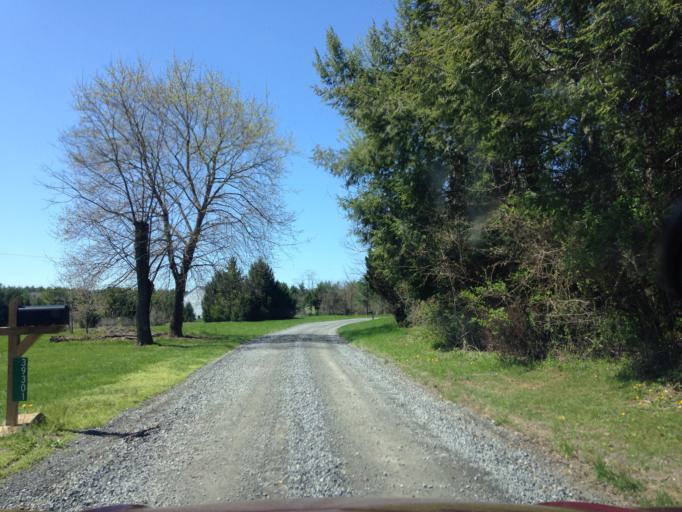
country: US
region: Maryland
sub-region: Frederick County
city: Brunswick
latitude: 39.2981
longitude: -77.6404
